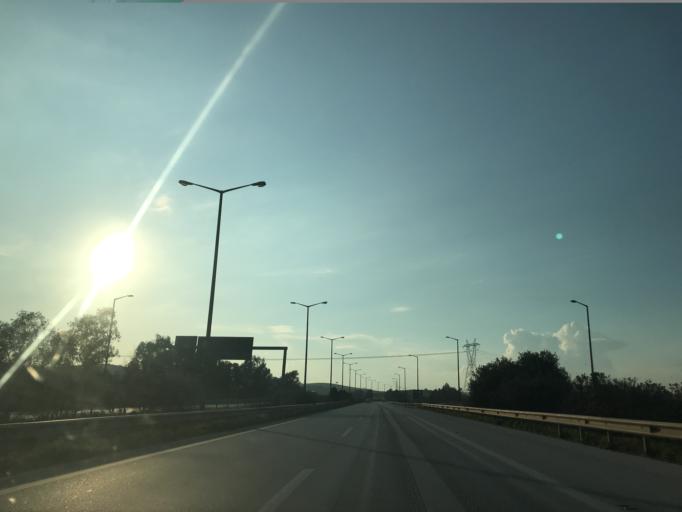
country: TR
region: Osmaniye
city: Toprakkale
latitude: 36.9754
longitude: 36.0157
